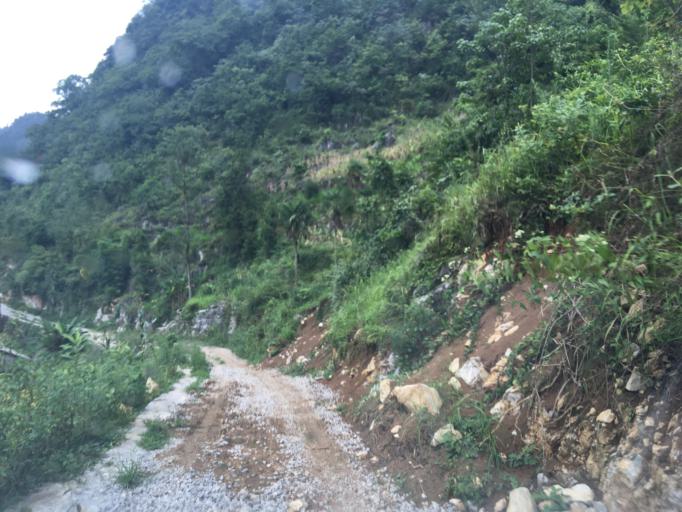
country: CN
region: Guangxi Zhuangzu Zizhiqu
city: Xinzhou
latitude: 25.2236
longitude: 105.6283
